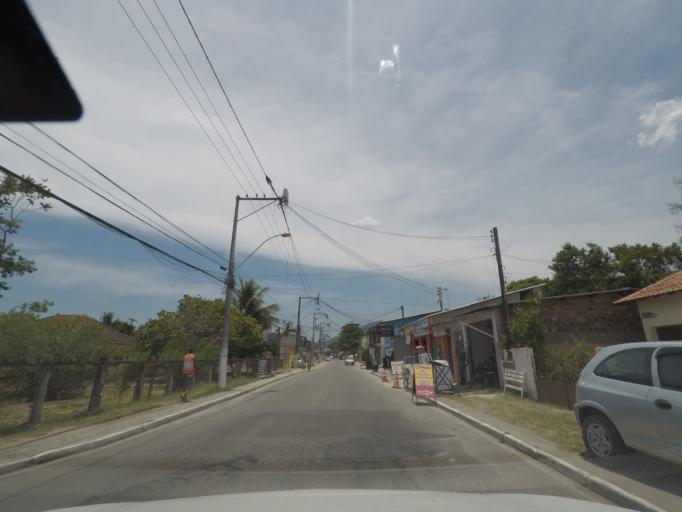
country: BR
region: Rio de Janeiro
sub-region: Marica
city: Marica
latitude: -22.9095
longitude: -42.8301
